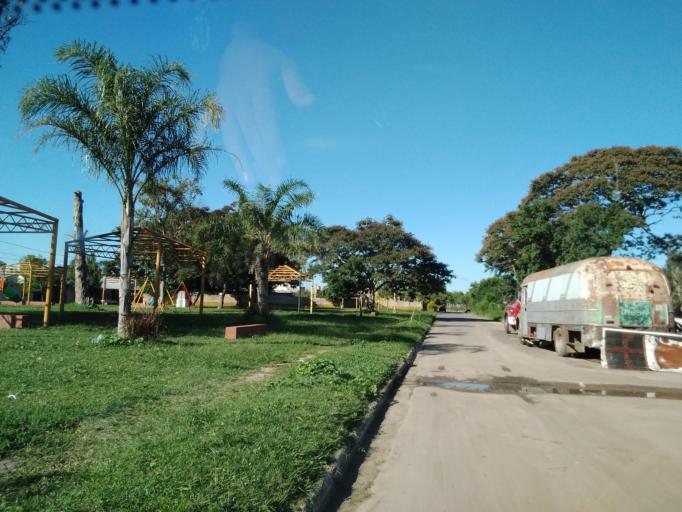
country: AR
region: Corrientes
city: Corrientes
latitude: -27.4586
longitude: -58.7677
